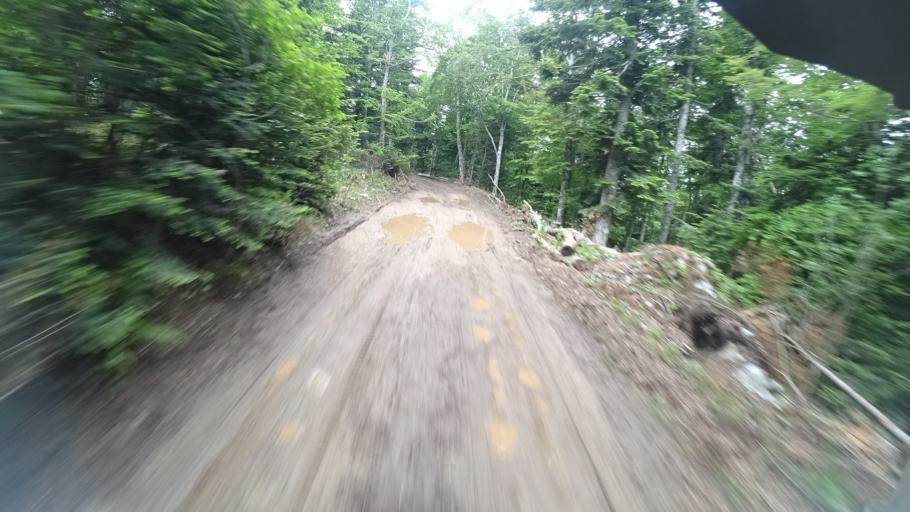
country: BA
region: Federation of Bosnia and Herzegovina
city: Bihac
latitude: 44.6904
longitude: 15.8305
